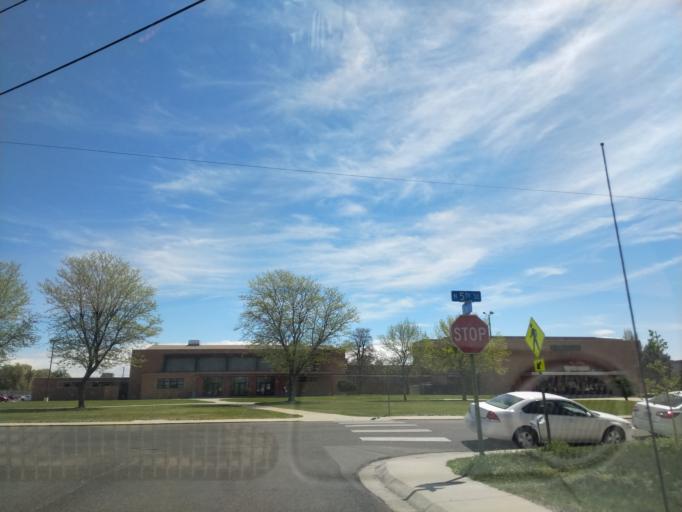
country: US
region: Colorado
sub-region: Mesa County
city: Grand Junction
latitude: 39.0808
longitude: -108.5647
